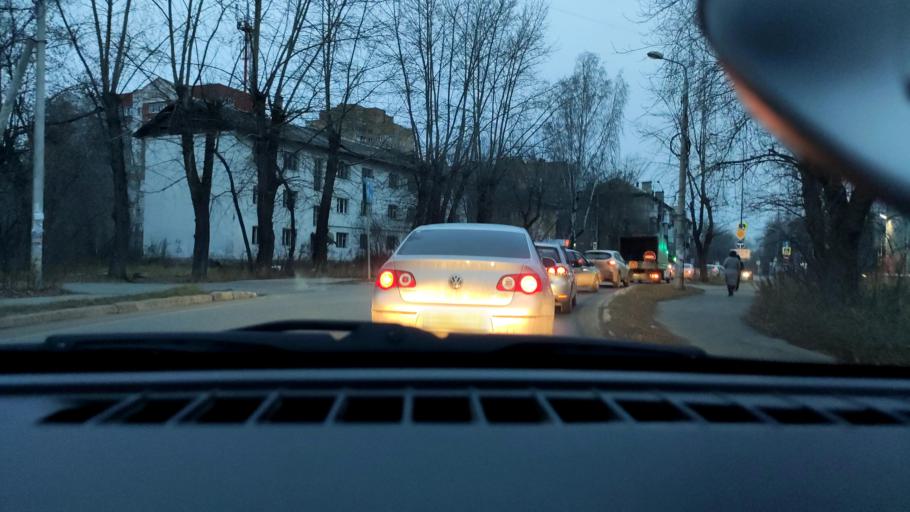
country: RU
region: Perm
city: Kondratovo
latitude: 57.9999
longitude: 56.1771
